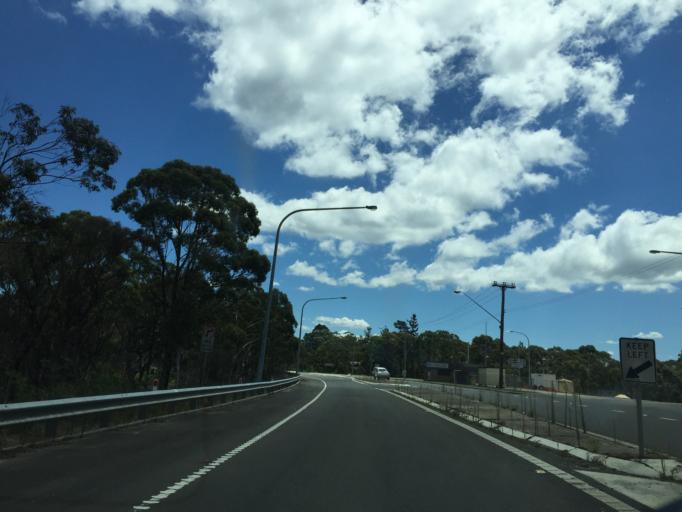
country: AU
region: New South Wales
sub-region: Blue Mountains Municipality
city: Blackheath
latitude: -33.5118
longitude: 150.2860
